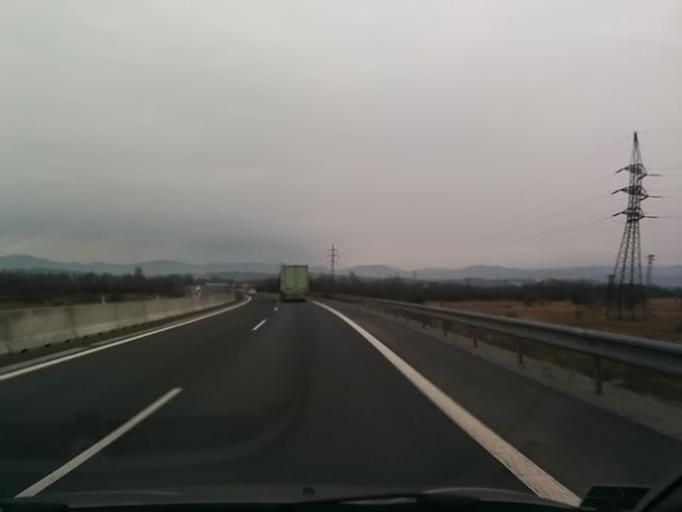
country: SK
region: Banskobystricky
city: Ziar nad Hronom
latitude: 48.5553
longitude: 18.8212
